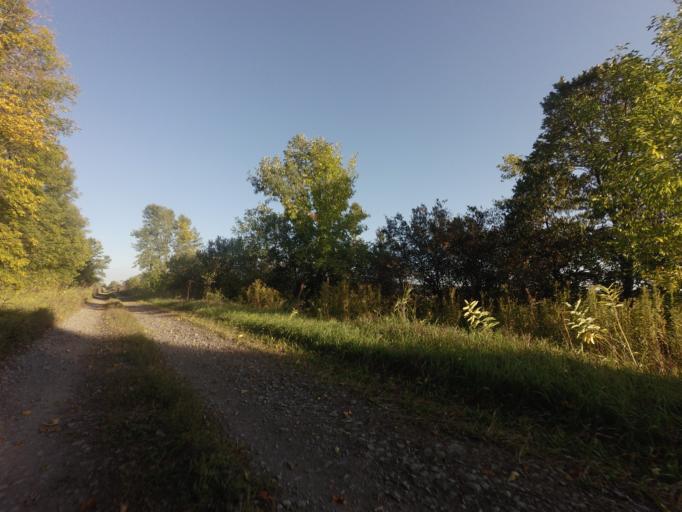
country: CA
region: Quebec
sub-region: Monteregie
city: Rigaud
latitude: 45.4848
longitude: -74.3517
